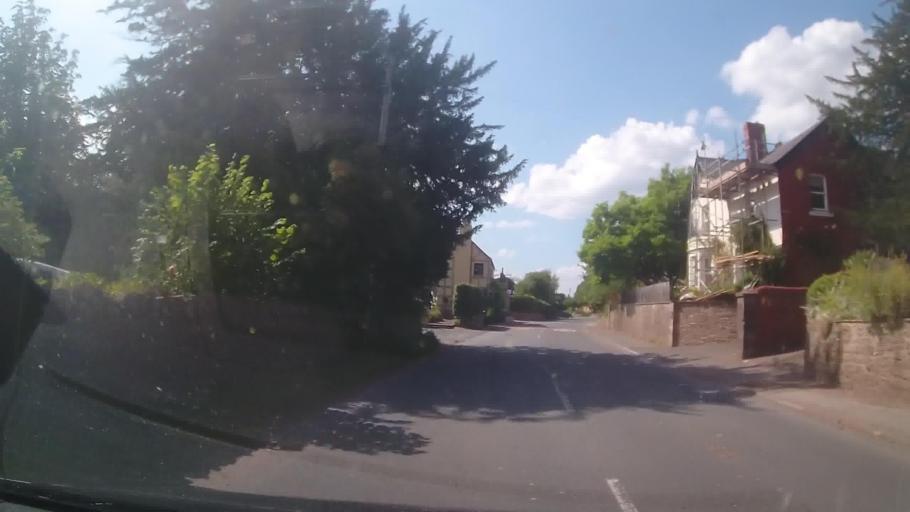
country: GB
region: England
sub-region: Herefordshire
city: Brockhampton
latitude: 52.0076
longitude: -2.6146
